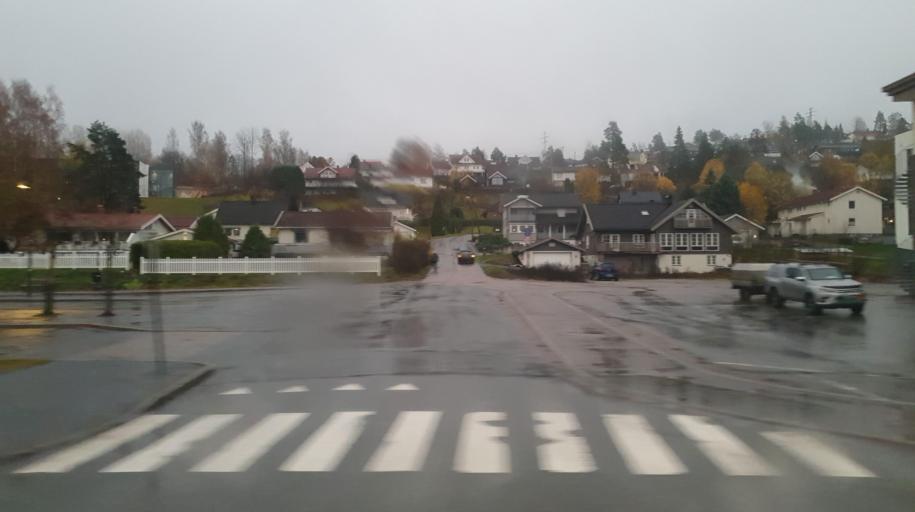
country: NO
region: Buskerud
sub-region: Modum
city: Vikersund
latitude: 59.8933
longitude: 9.9273
